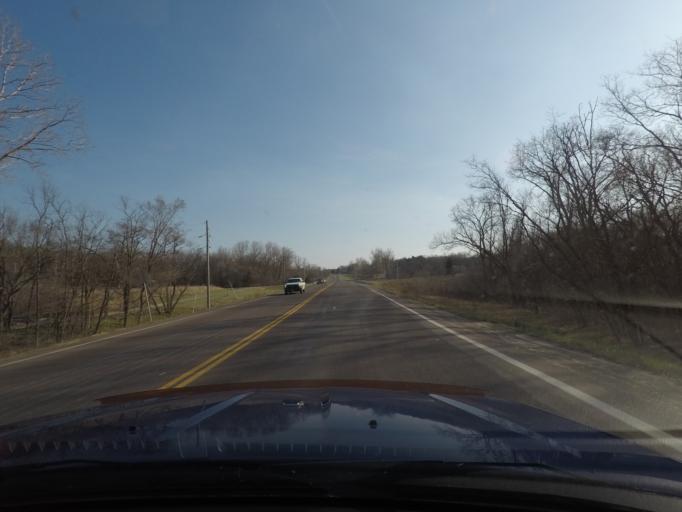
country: US
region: Kansas
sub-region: Douglas County
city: Lawrence
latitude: 39.0456
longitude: -95.3897
